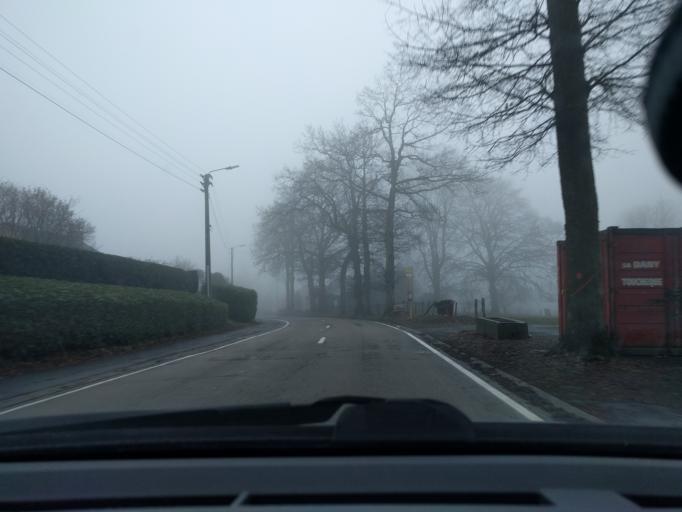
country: BE
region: Wallonia
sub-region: Province du Luxembourg
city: Gouvy
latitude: 50.1963
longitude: 5.9237
